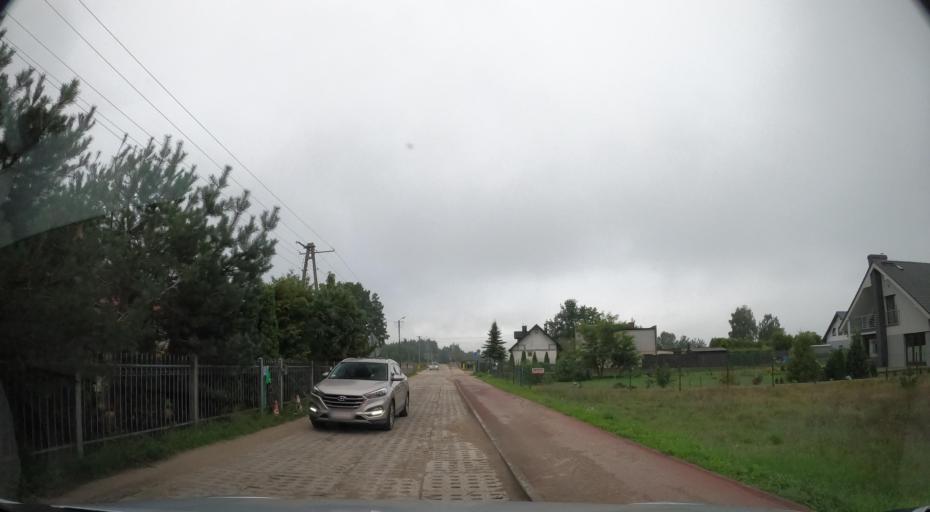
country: PL
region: Pomeranian Voivodeship
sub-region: Powiat kartuski
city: Chwaszczyno
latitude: 54.4287
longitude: 18.4161
